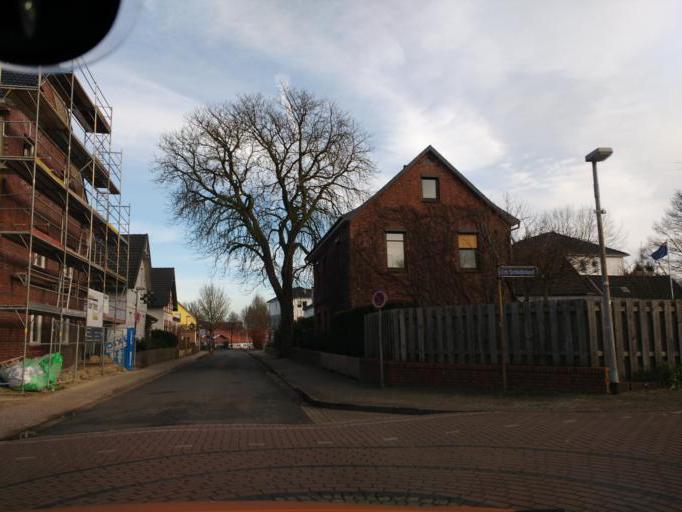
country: DE
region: Lower Saxony
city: Hude
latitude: 53.1080
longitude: 8.4601
